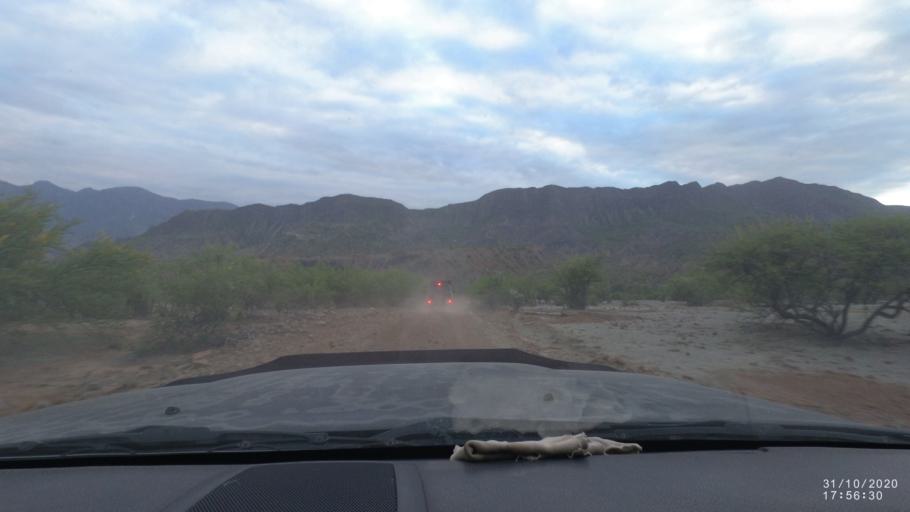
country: BO
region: Chuquisaca
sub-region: Provincia Zudanez
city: Mojocoya
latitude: -18.6482
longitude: -64.5302
